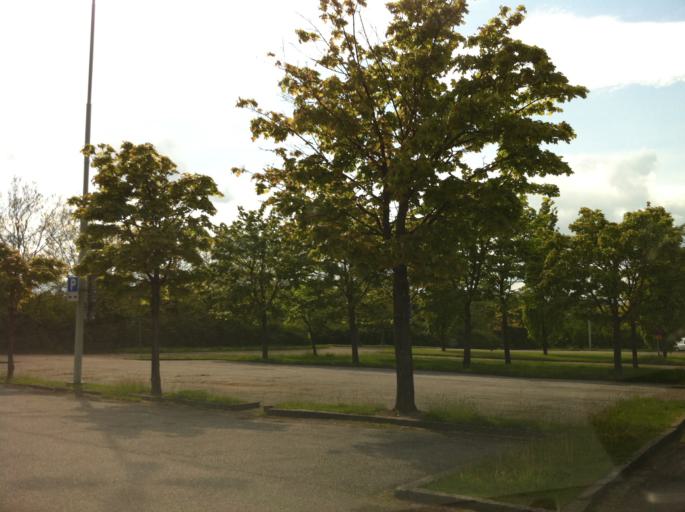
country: SE
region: Skane
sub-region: Landskrona
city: Landskrona
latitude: 55.8924
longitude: 12.8427
